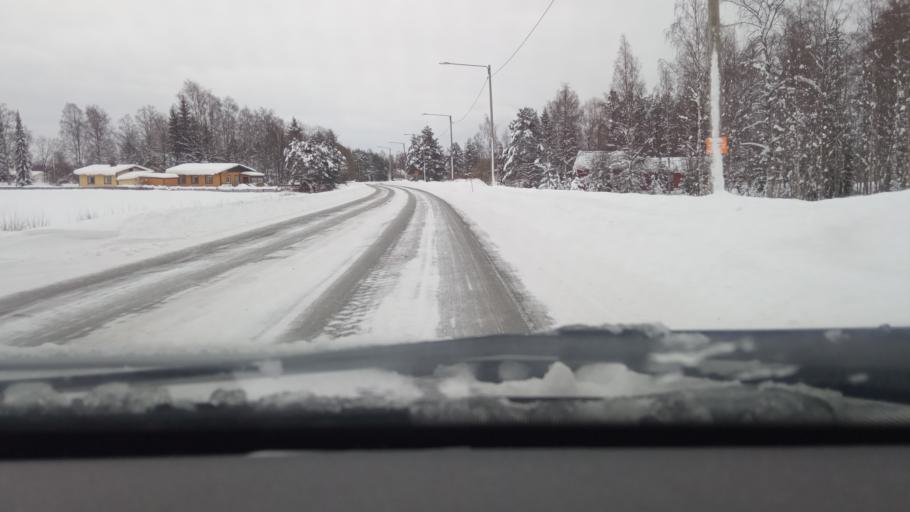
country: FI
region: Southern Ostrobothnia
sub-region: Jaerviseutu
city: Alajaervi
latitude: 62.9934
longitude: 23.8275
